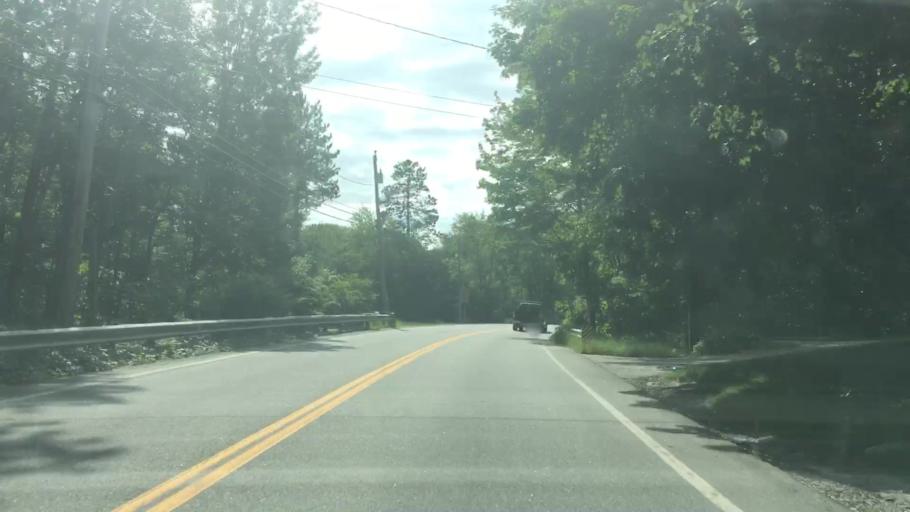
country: US
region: Maine
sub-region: Cumberland County
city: Raymond
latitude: 43.9857
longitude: -70.4805
